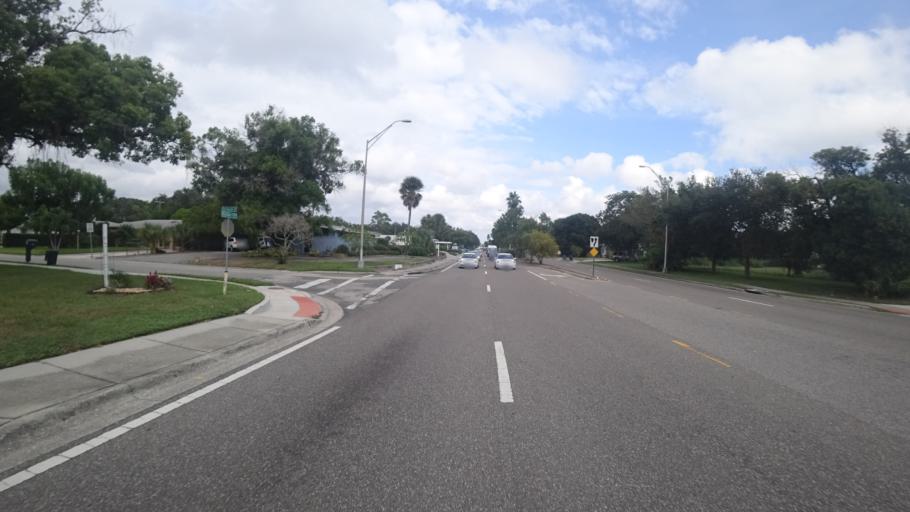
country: US
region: Florida
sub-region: Manatee County
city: Bayshore Gardens
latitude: 27.4313
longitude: -82.5811
